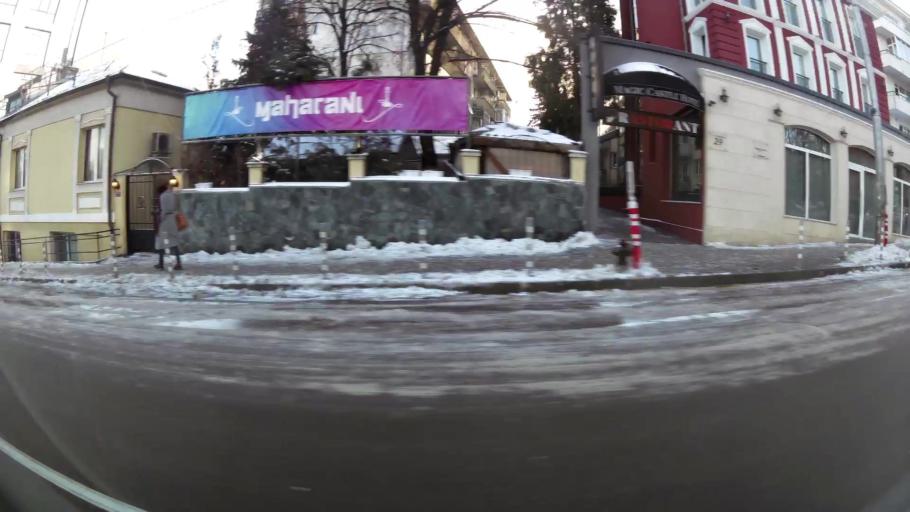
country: BG
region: Sofia-Capital
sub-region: Stolichna Obshtina
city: Sofia
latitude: 42.6771
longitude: 23.3220
